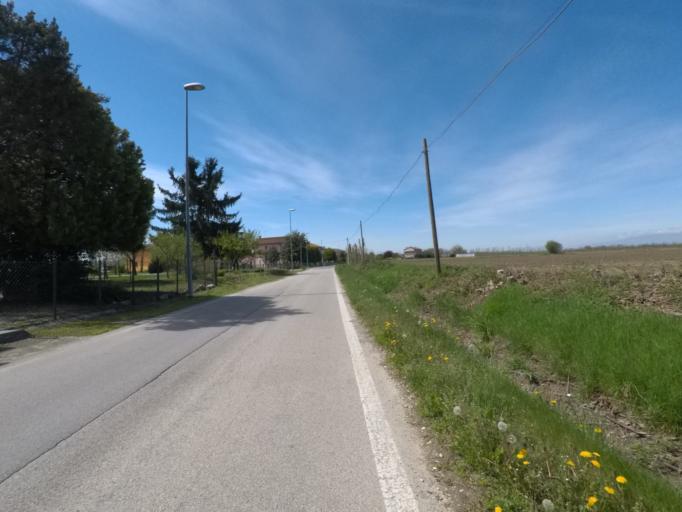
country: IT
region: Friuli Venezia Giulia
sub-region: Provincia di Udine
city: Camino al Tagliamento
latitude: 45.9533
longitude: 12.9286
